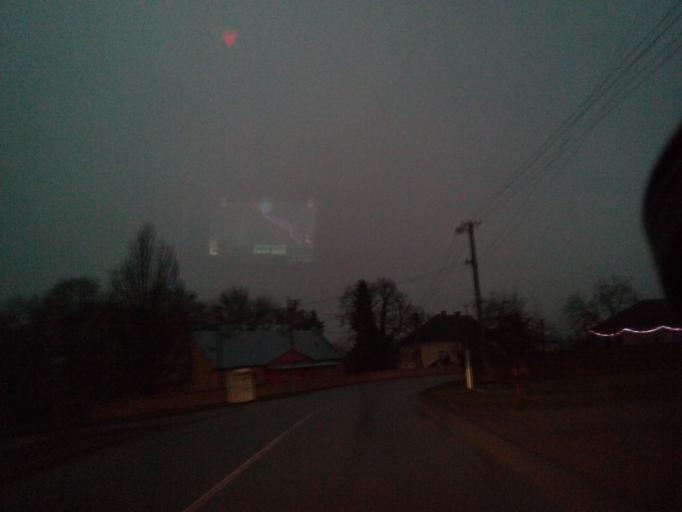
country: SK
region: Presovsky
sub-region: Okres Presov
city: Presov
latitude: 49.0125
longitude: 21.1857
